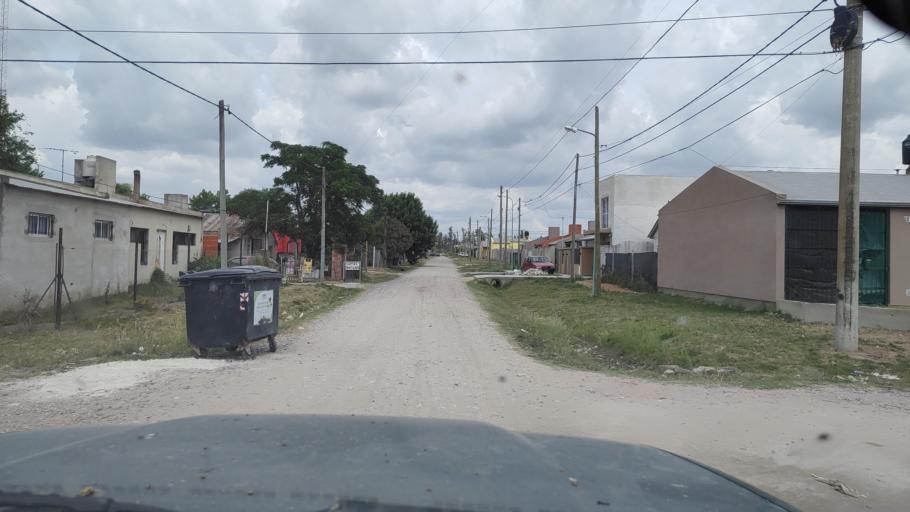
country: AR
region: Buenos Aires
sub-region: Partido de Lujan
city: Lujan
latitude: -34.5543
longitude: -59.1345
